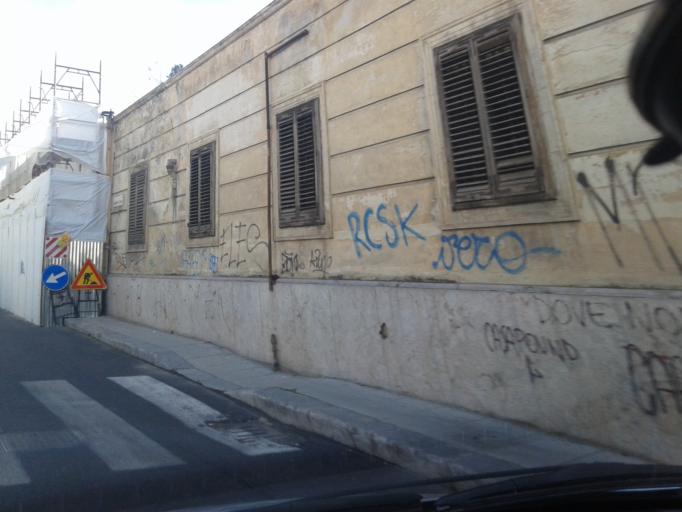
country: IT
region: Sicily
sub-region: Palermo
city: Palermo
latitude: 38.1182
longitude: 13.3428
